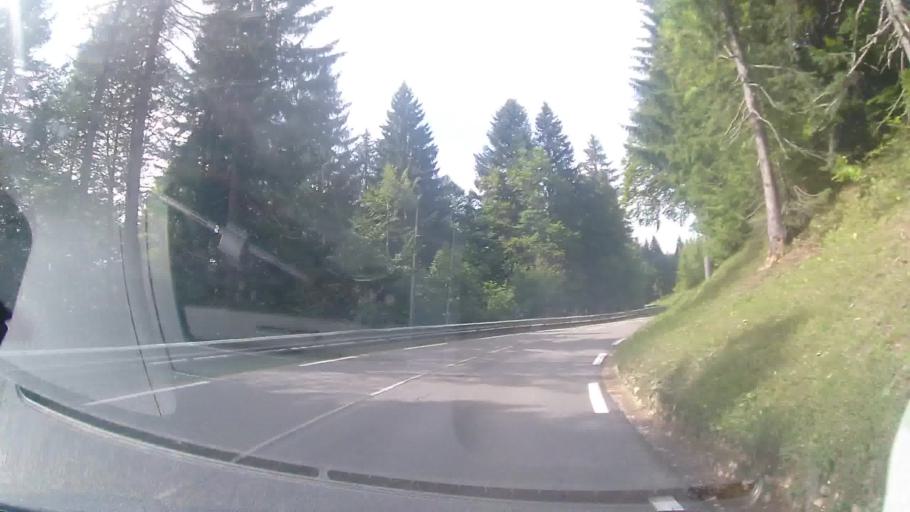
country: FR
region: Franche-Comte
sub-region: Departement du Jura
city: Les Rousses
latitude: 46.4130
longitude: 6.0614
